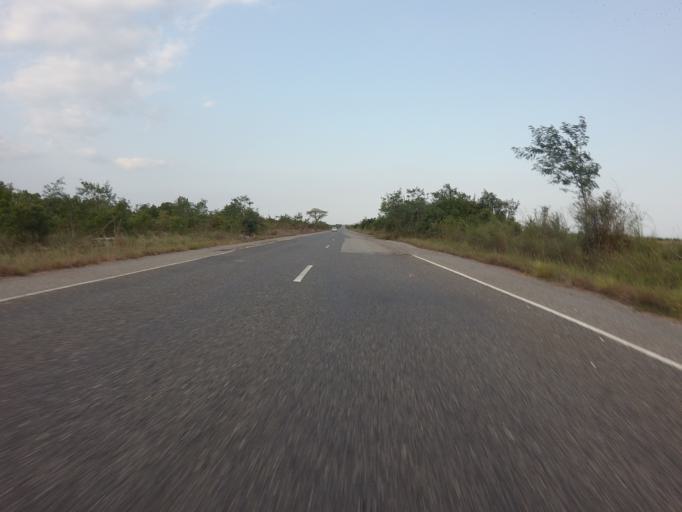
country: GH
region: Volta
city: Anloga
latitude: 6.0842
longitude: 0.5593
